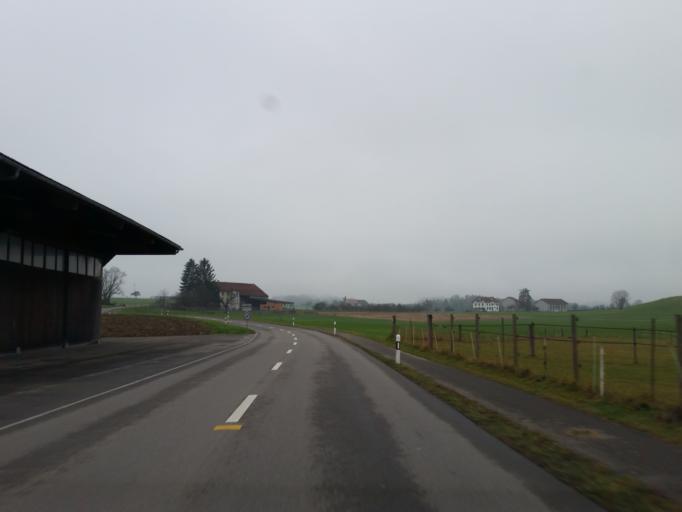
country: CH
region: Thurgau
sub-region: Weinfelden District
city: Erlen
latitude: 47.5368
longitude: 9.2305
